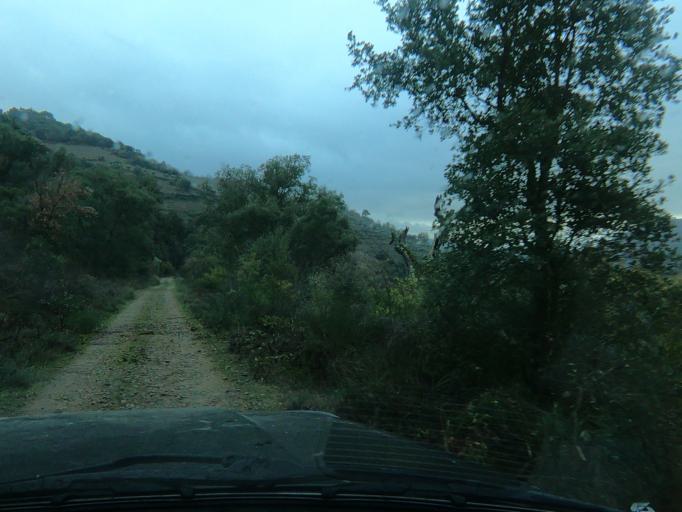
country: PT
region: Vila Real
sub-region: Santa Marta de Penaguiao
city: Santa Marta de Penaguiao
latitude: 41.2102
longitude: -7.7611
